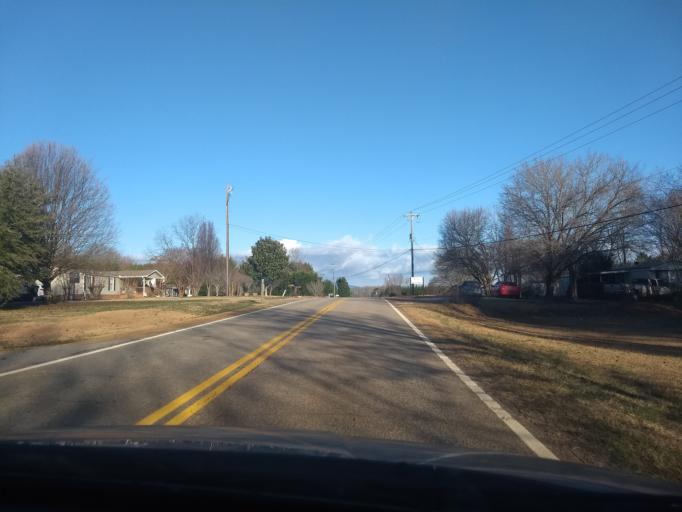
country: US
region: South Carolina
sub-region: Greenville County
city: Greer
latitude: 34.9861
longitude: -82.2010
